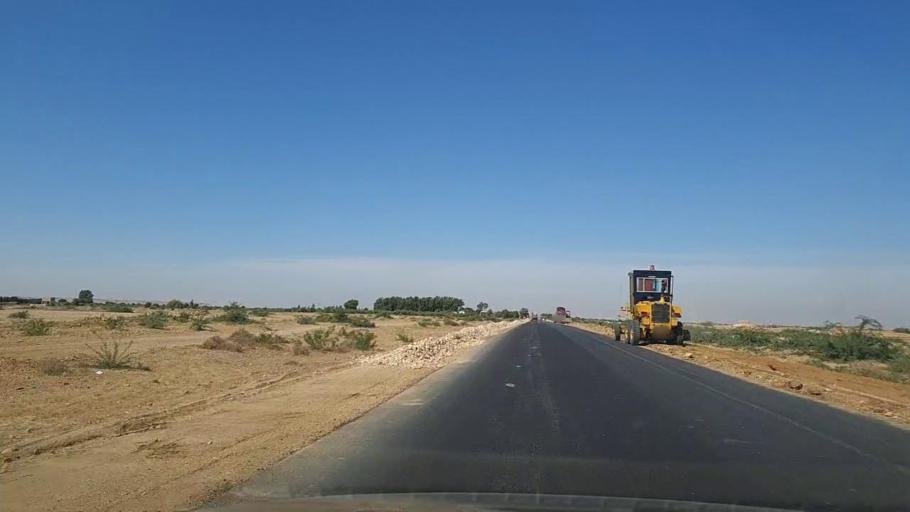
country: PK
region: Sindh
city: Kotri
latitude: 25.2594
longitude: 68.2231
